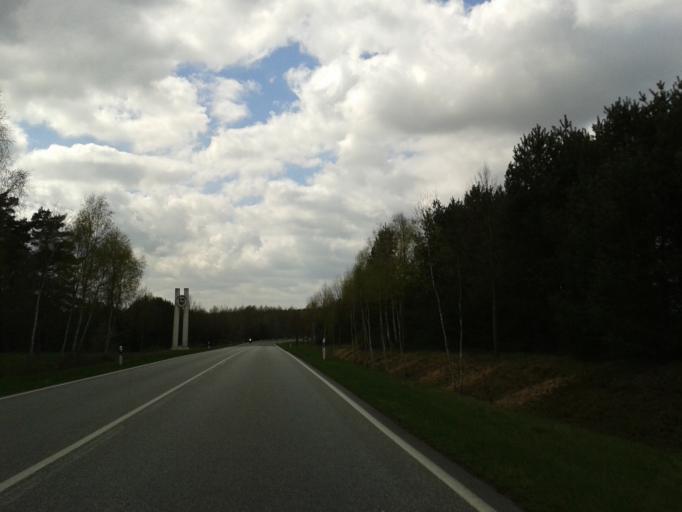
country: DE
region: Lower Saxony
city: Bergen an der Dumme
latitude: 52.8839
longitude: 10.9923
